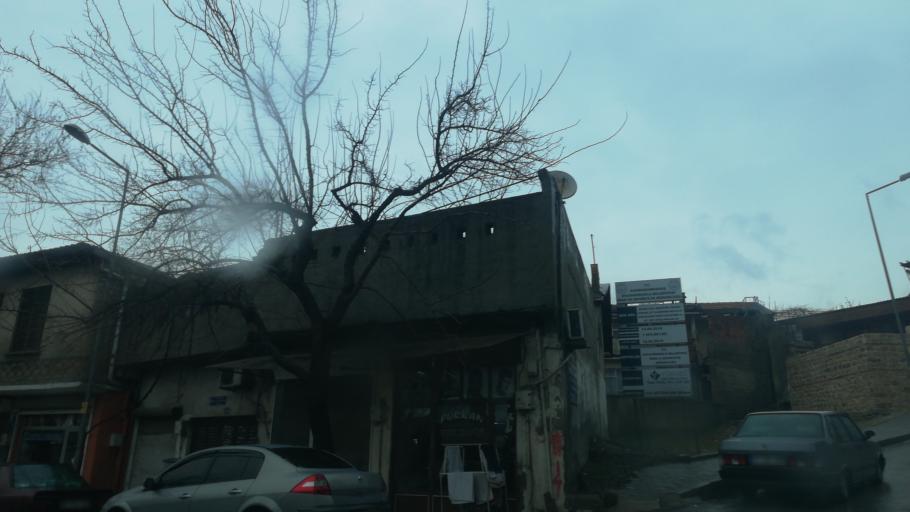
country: TR
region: Kahramanmaras
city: Kahramanmaras
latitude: 37.5844
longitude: 36.9303
